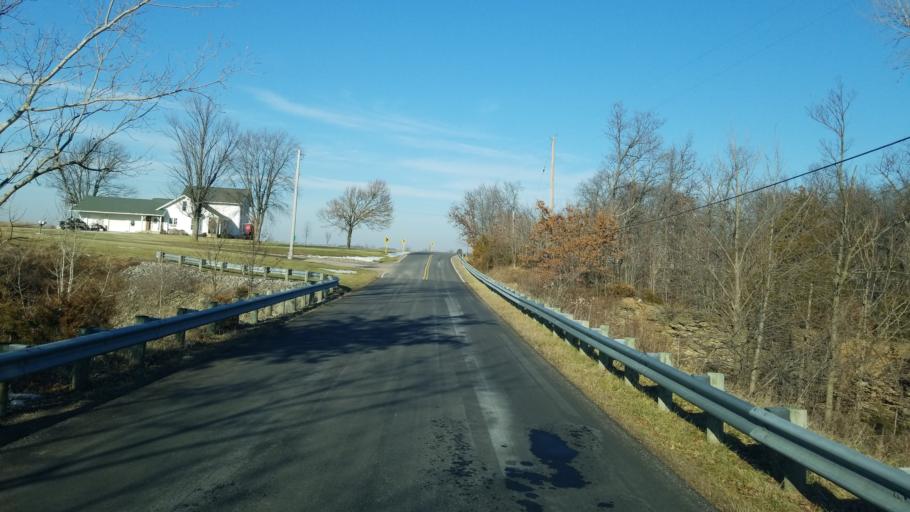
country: US
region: Ohio
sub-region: Huron County
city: Monroeville
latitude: 41.2758
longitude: -82.6837
